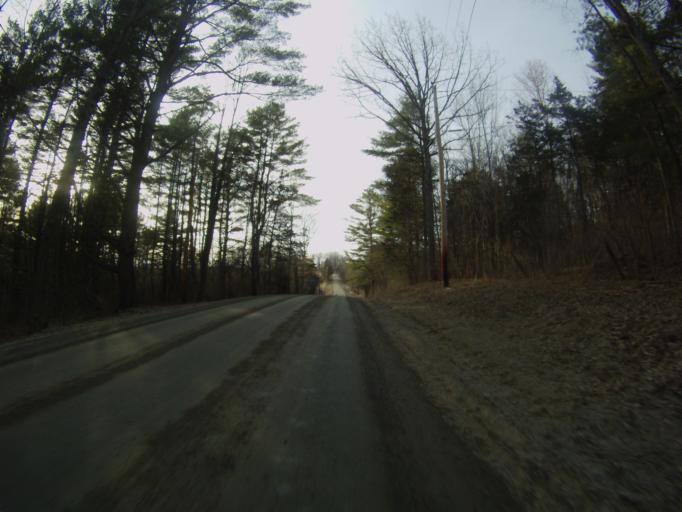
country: US
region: Vermont
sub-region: Addison County
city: Middlebury (village)
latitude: 44.0388
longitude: -73.2771
